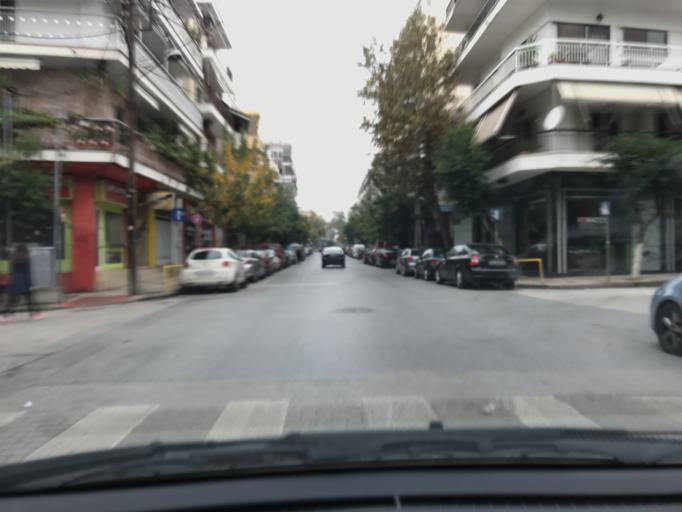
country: GR
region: Central Macedonia
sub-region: Nomos Thessalonikis
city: Ampelokipoi
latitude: 40.6537
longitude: 22.9248
